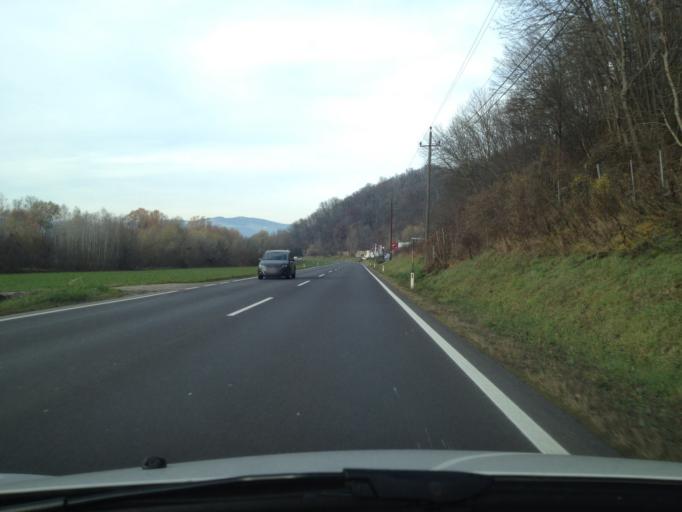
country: AT
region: Upper Austria
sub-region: Politischer Bezirk Urfahr-Umgebung
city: Steyregg
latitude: 48.3001
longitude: 14.3422
